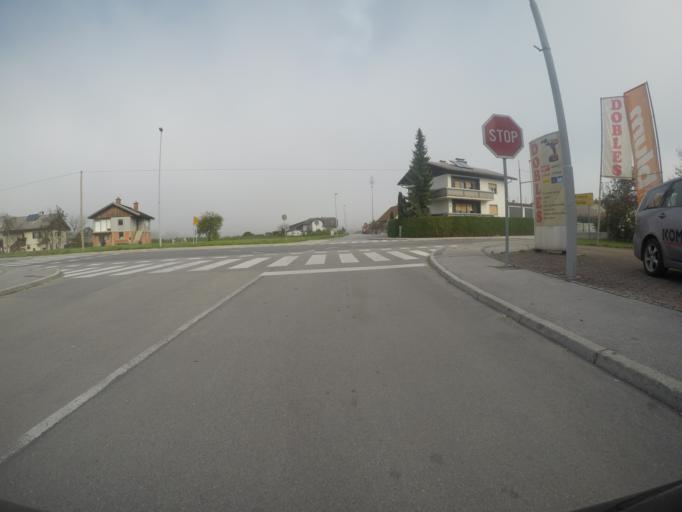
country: SI
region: Domzale
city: Dob
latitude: 46.1538
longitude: 14.6281
